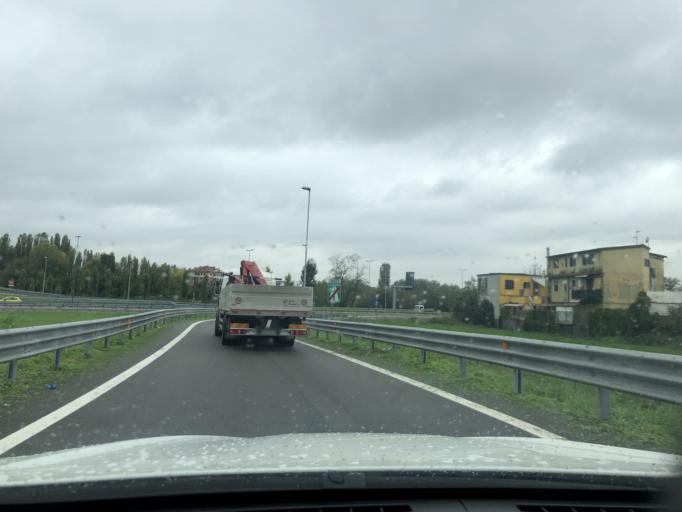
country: IT
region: Lombardy
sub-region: Citta metropolitana di Milano
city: Cesano Boscone
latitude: 45.4580
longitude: 9.0756
